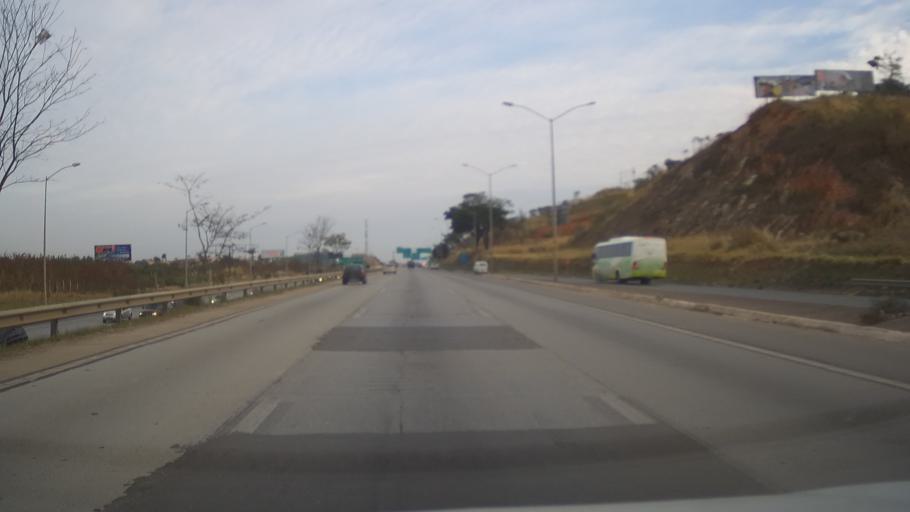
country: BR
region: Minas Gerais
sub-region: Vespasiano
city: Vespasiano
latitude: -19.7683
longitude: -43.9483
